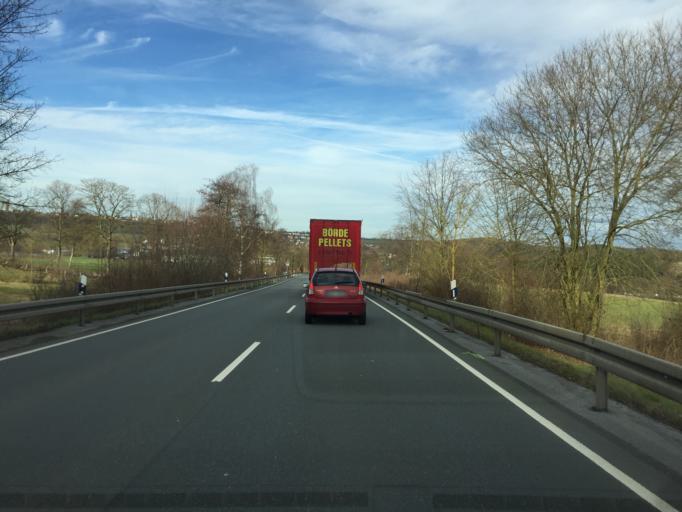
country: DE
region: North Rhine-Westphalia
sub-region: Regierungsbezirk Arnsberg
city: Ruthen
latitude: 51.4741
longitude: 8.4473
